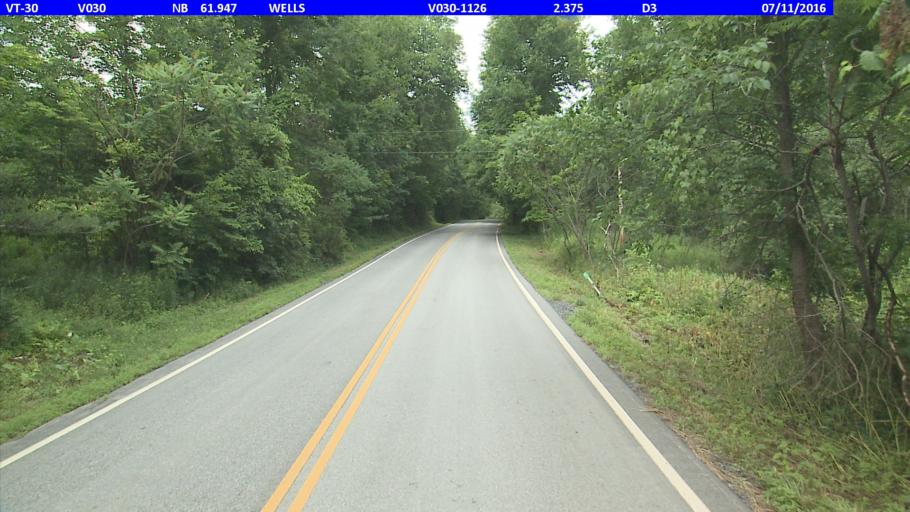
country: US
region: New York
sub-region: Washington County
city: Granville
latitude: 43.4284
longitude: -73.1960
